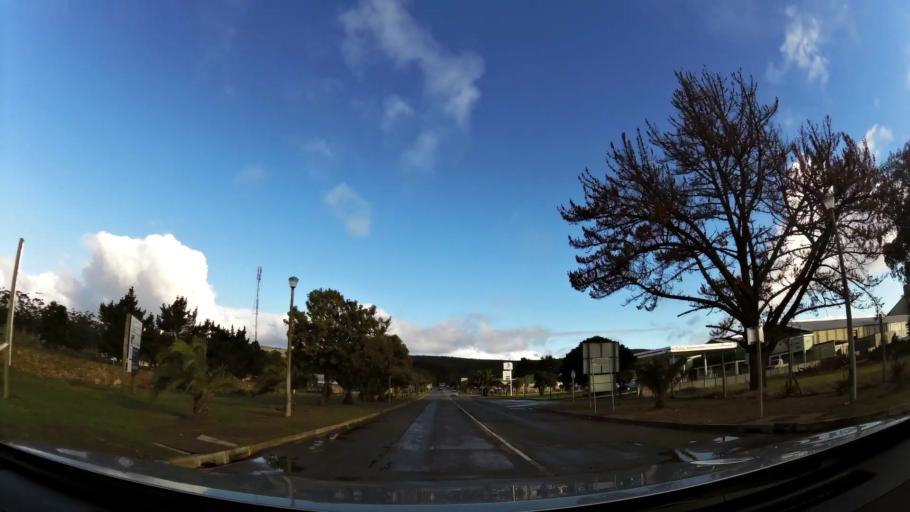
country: ZA
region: Western Cape
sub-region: Eden District Municipality
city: Riversdale
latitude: -34.2097
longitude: 21.5849
